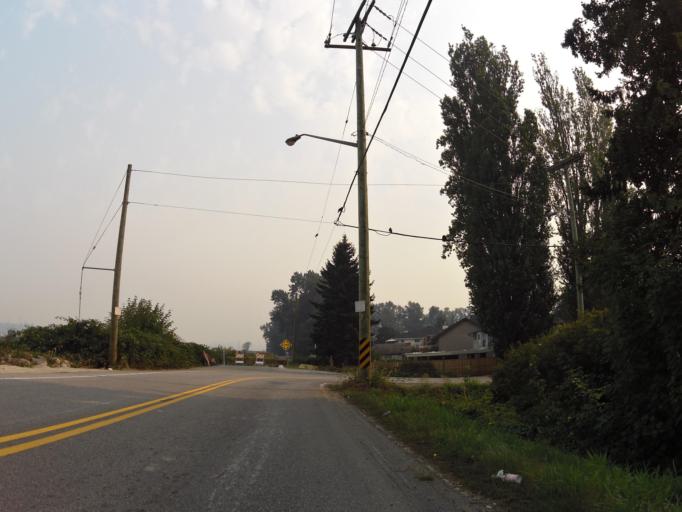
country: CA
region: British Columbia
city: New Westminster
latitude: 49.1815
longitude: -122.9663
